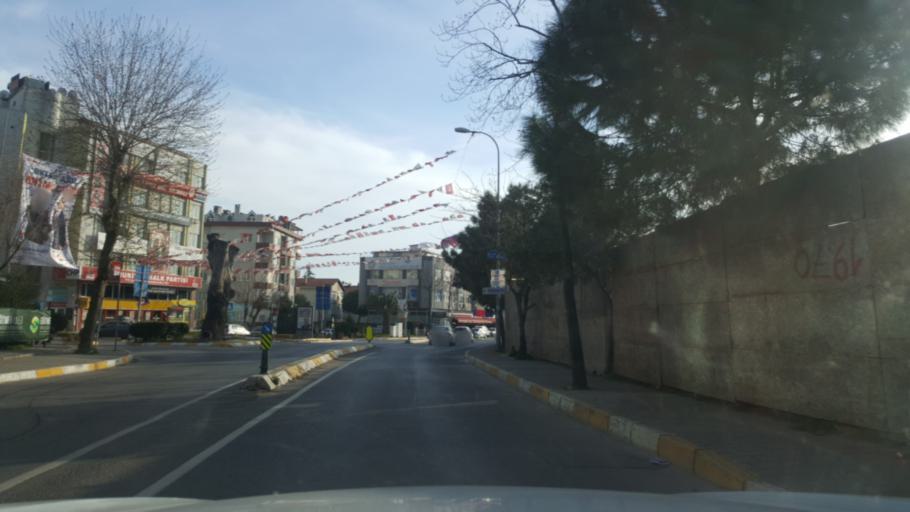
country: TR
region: Istanbul
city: Icmeler
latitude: 40.8224
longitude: 29.3096
